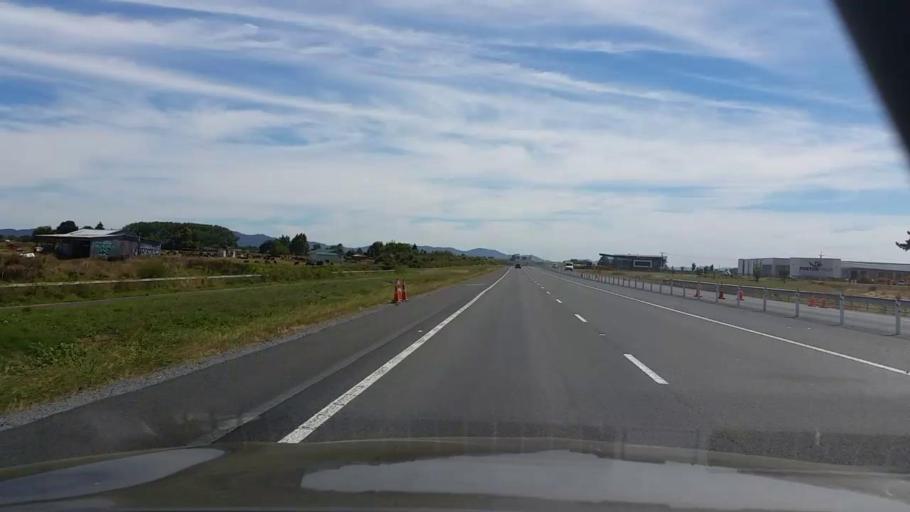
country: NZ
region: Waikato
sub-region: Hamilton City
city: Hamilton
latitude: -37.7451
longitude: 175.2145
